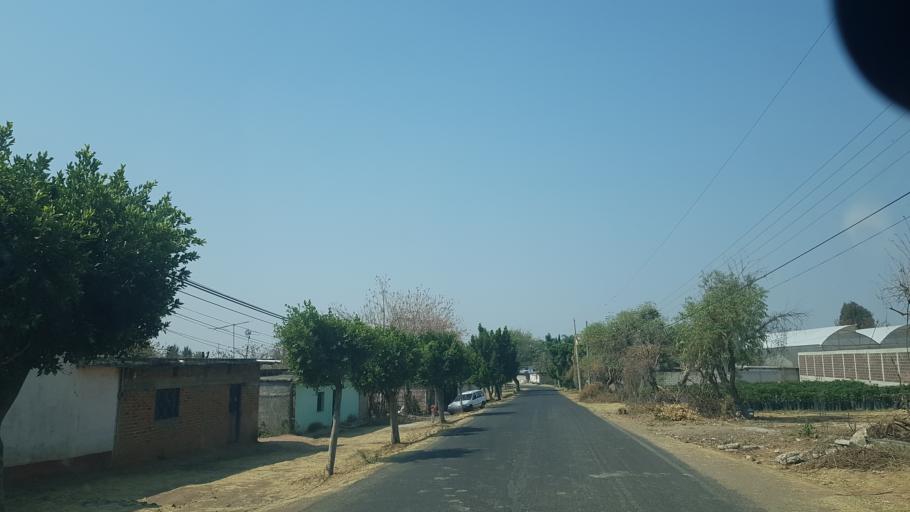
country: MX
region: Morelos
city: Tlacotepec
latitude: 18.8196
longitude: -98.7439
